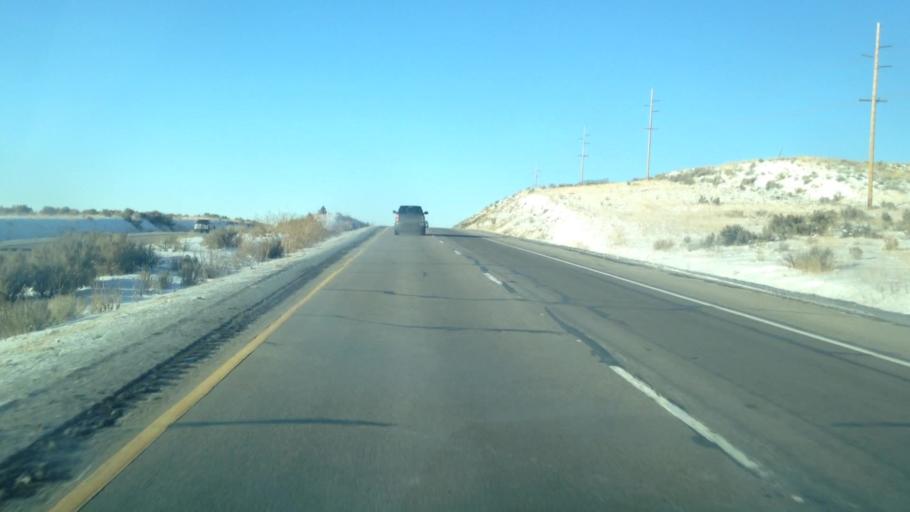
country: US
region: Idaho
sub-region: Bannock County
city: Pocatello
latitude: 42.8571
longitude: -112.4173
